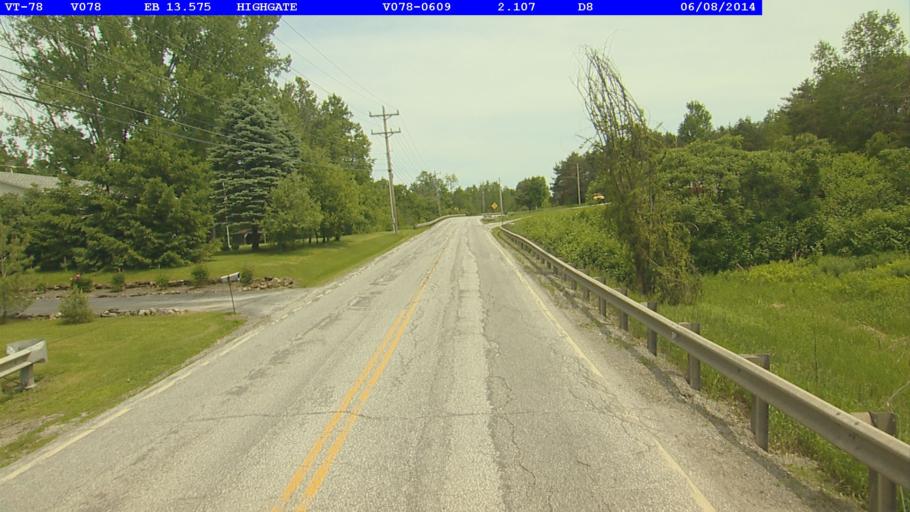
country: US
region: Vermont
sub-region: Franklin County
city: Swanton
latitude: 44.9401
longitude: -73.0628
